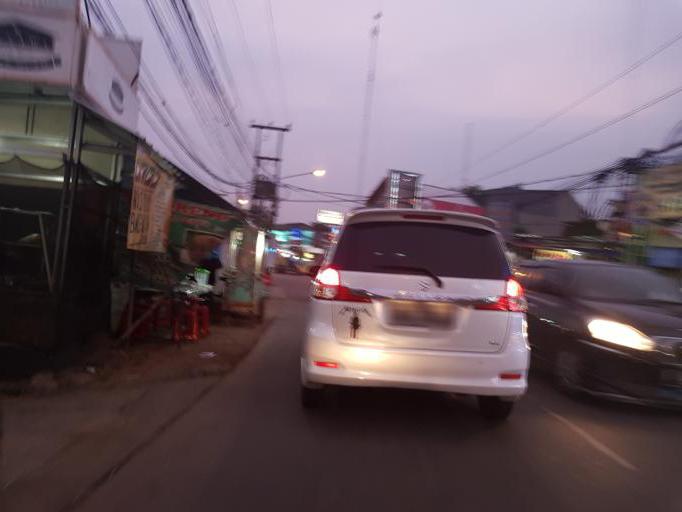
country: ID
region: West Java
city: Bekasi
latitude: -6.2954
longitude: 106.9204
